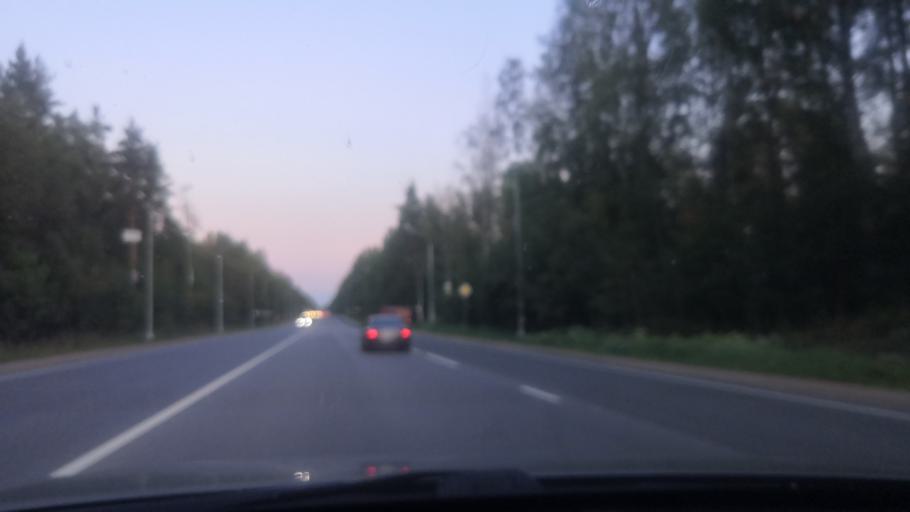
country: RU
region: St.-Petersburg
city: Pesochnyy
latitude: 60.1884
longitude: 30.1015
